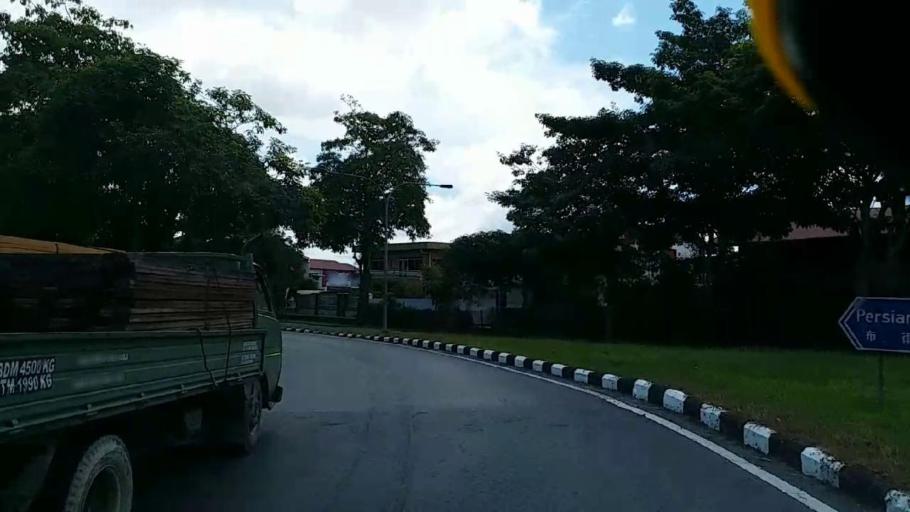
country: MY
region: Sarawak
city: Sibu
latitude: 2.3009
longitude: 111.8363
